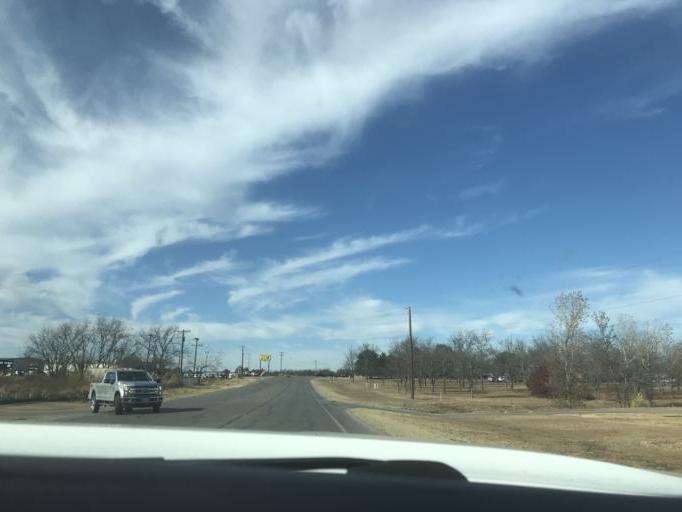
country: US
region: Texas
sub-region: Erath County
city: Stephenville
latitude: 32.2034
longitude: -98.2466
